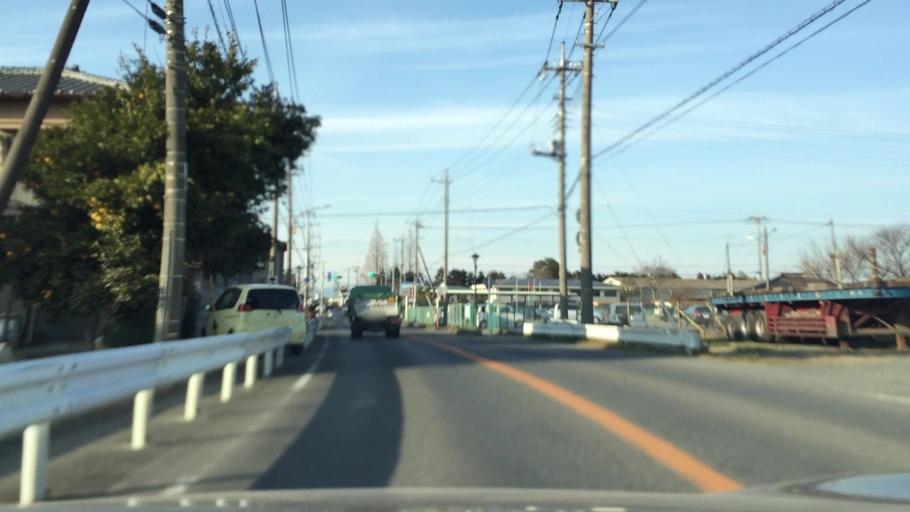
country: JP
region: Saitama
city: Menuma
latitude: 36.2115
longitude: 139.3785
